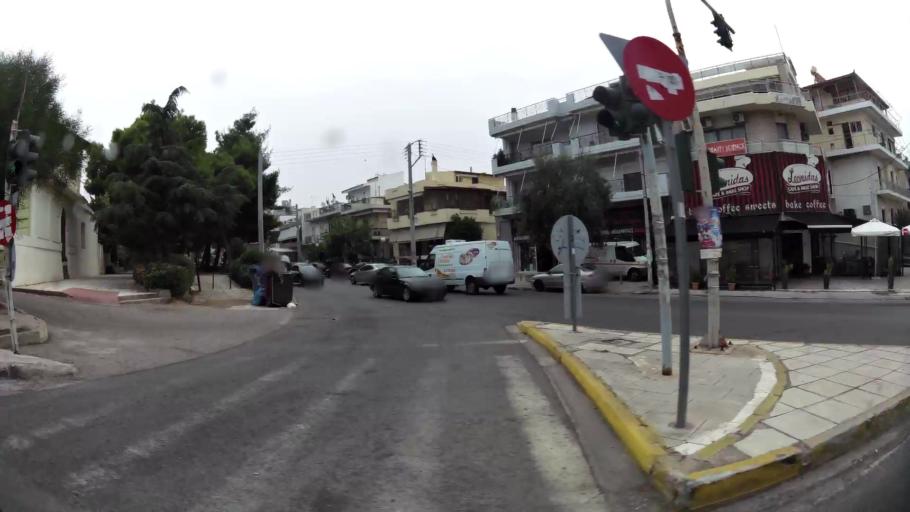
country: GR
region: Attica
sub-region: Nomarchia Athinas
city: Chaidari
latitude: 38.0007
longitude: 23.6627
